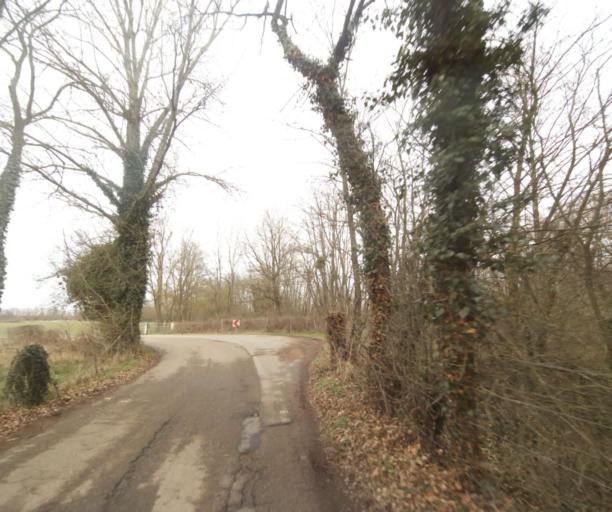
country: FR
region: Rhone-Alpes
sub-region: Departement de la Loire
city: Perreux
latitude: 46.0631
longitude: 4.1051
